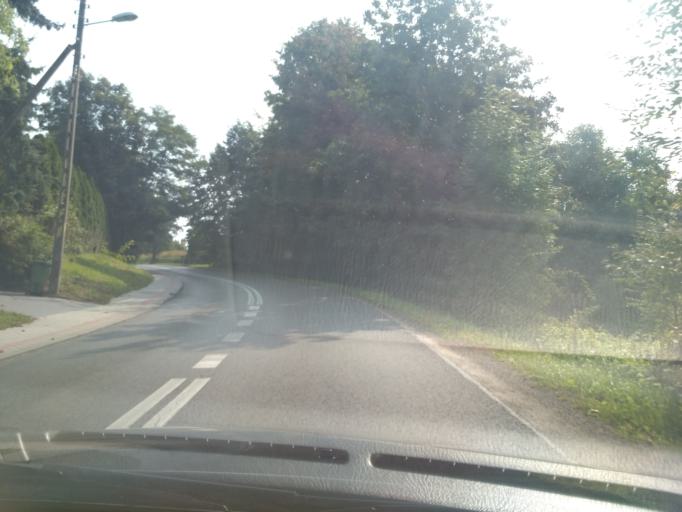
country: PL
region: Subcarpathian Voivodeship
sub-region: Powiat rzeszowski
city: Boguchwala
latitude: 50.0030
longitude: 21.9374
